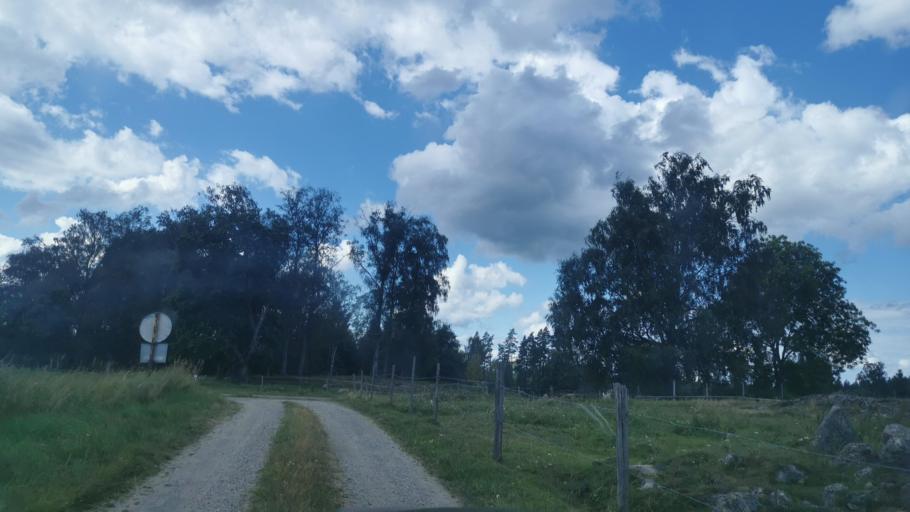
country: SE
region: OEstergoetland
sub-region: Finspangs Kommun
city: Finspang
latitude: 58.8000
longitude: 15.7764
